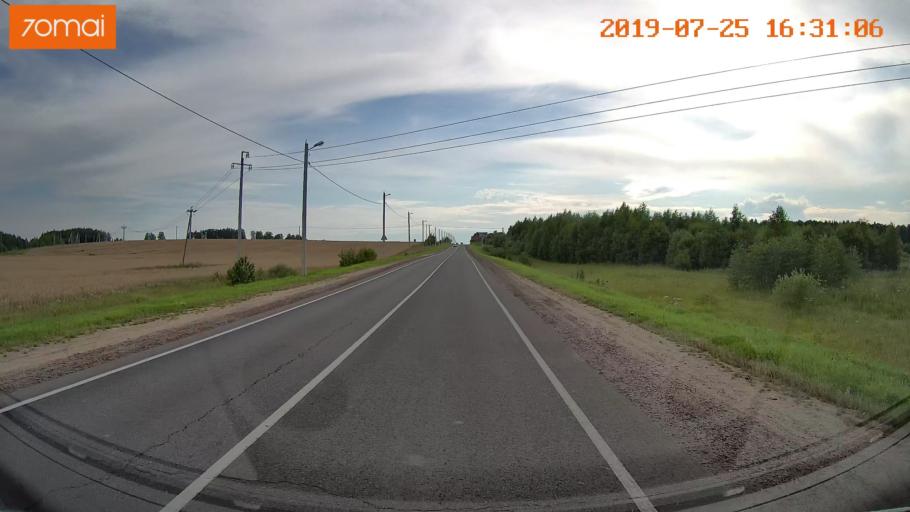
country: RU
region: Ivanovo
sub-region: Privolzhskiy Rayon
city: Ples
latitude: 57.4455
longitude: 41.4906
